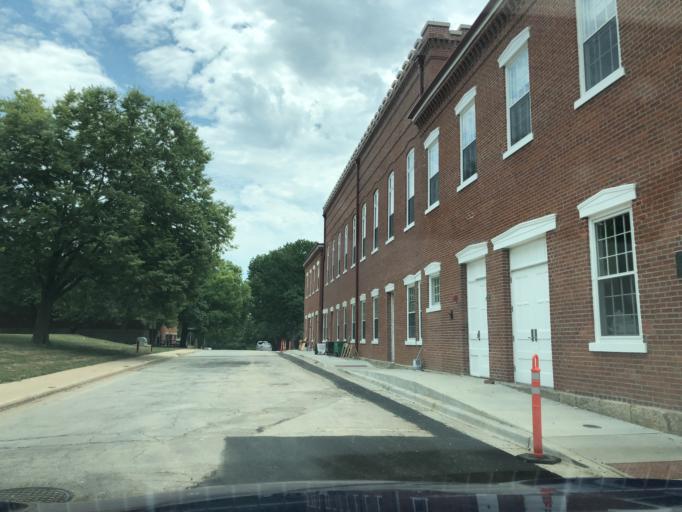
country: US
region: Kansas
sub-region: Leavenworth County
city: Leavenworth
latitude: 39.3506
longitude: -94.9154
